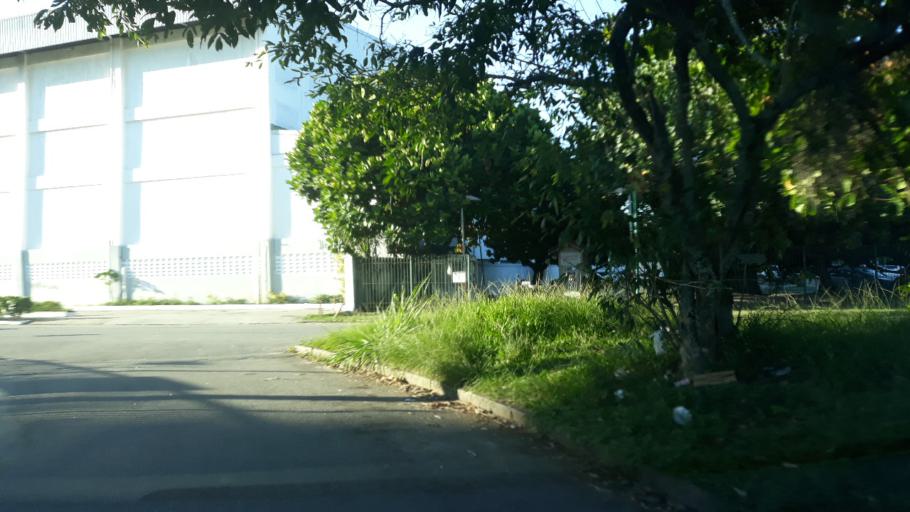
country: BR
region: Rio de Janeiro
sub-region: Rio De Janeiro
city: Rio de Janeiro
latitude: -23.0023
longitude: -43.3374
